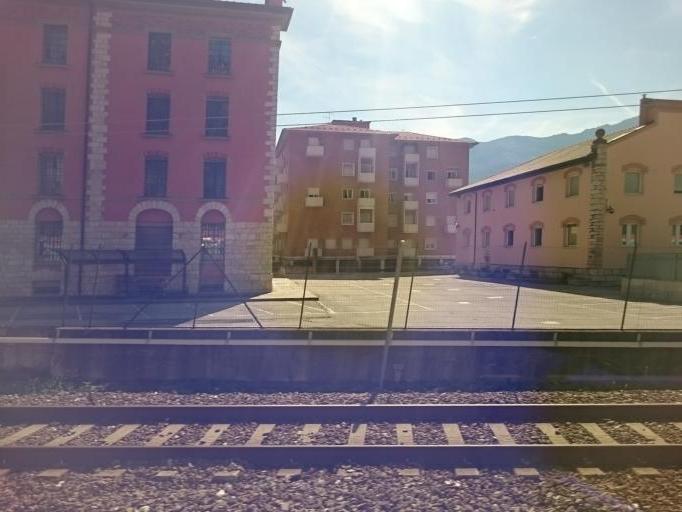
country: IT
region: Trentino-Alto Adige
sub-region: Provincia di Trento
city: Trento
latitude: 46.0658
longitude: 11.1155
